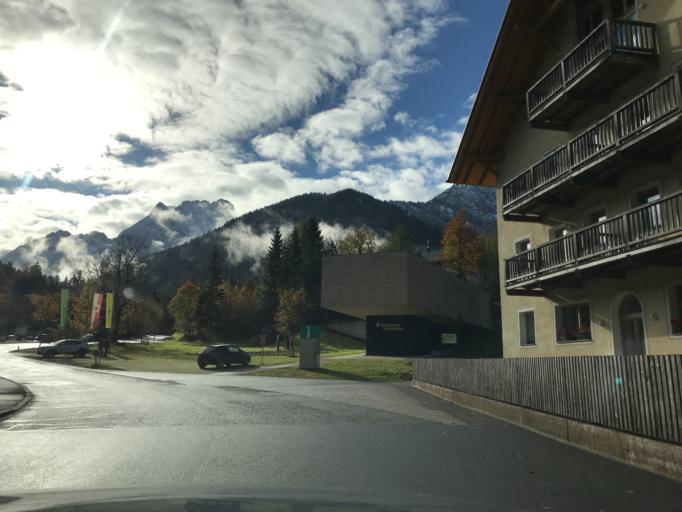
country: DE
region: Bavaria
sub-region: Upper Bavaria
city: Jachenau
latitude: 47.4736
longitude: 11.4655
